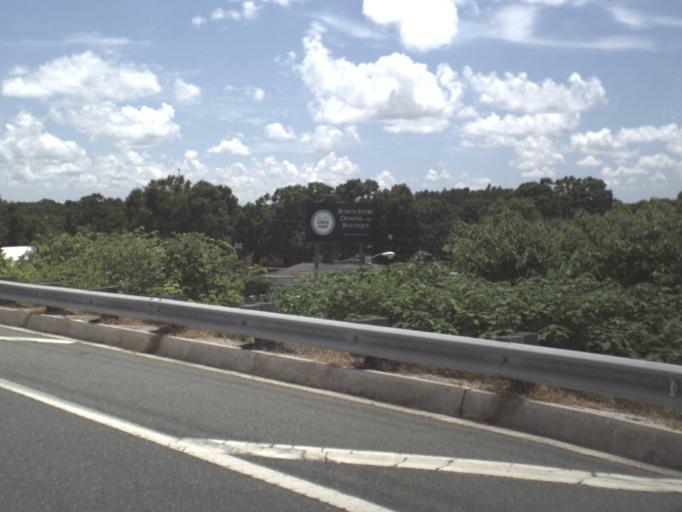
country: US
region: Florida
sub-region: Hillsborough County
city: Egypt Lake-Leto
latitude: 28.0358
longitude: -82.5050
